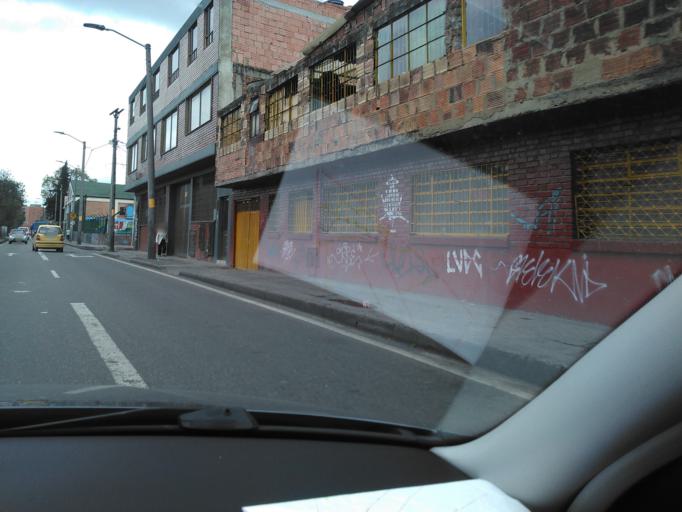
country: CO
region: Bogota D.C.
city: Bogota
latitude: 4.6222
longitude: -74.1220
